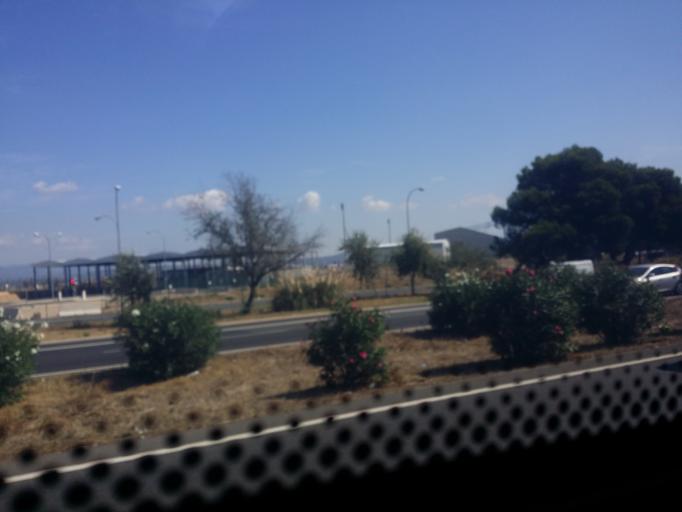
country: ES
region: Balearic Islands
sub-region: Illes Balears
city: s'Arenal
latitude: 39.5426
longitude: 2.7109
